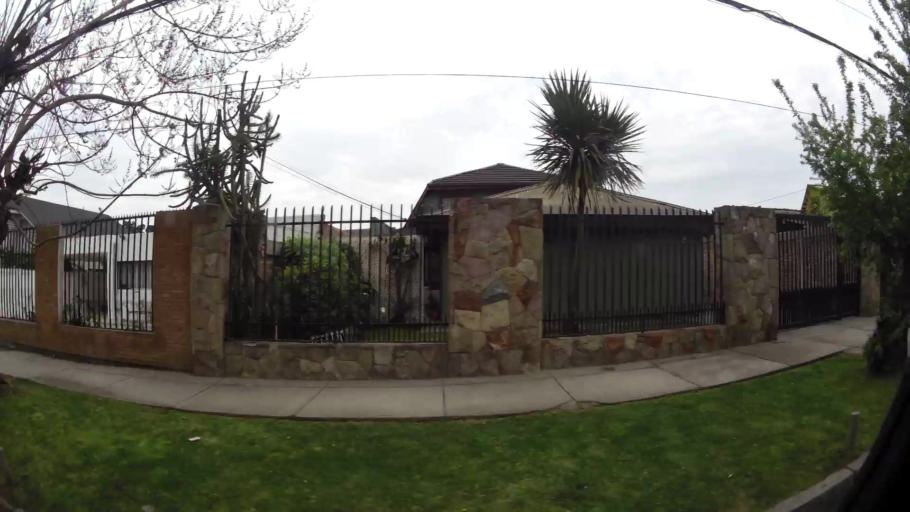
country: CL
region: Santiago Metropolitan
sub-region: Provincia de Santiago
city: Lo Prado
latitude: -33.5055
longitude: -70.7542
